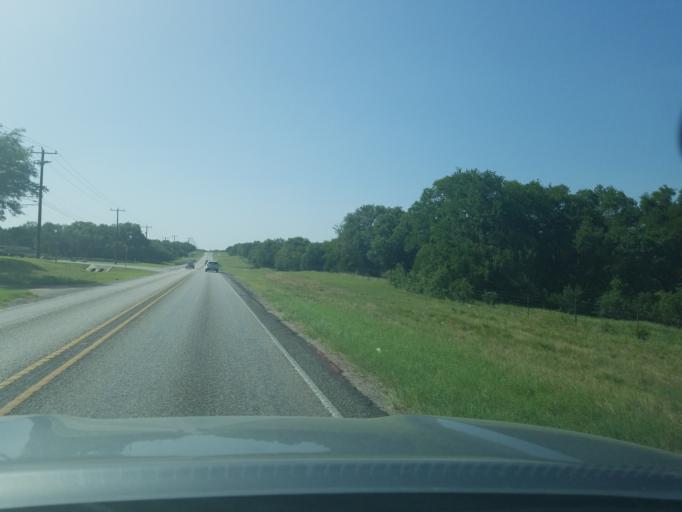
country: US
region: Texas
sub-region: Comal County
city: Garden Ridge
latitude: 29.6809
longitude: -98.3239
